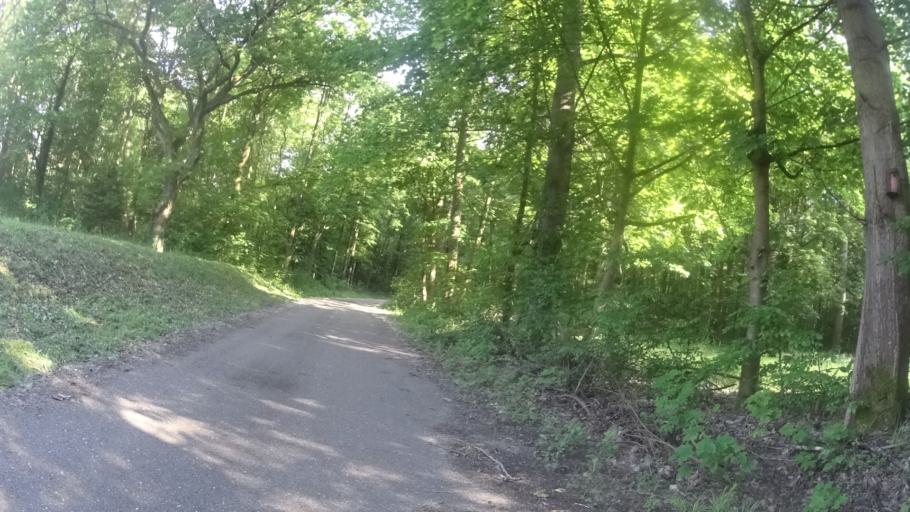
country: DE
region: Baden-Wuerttemberg
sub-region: Karlsruhe Region
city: Greffern
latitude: 48.7516
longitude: 7.9892
